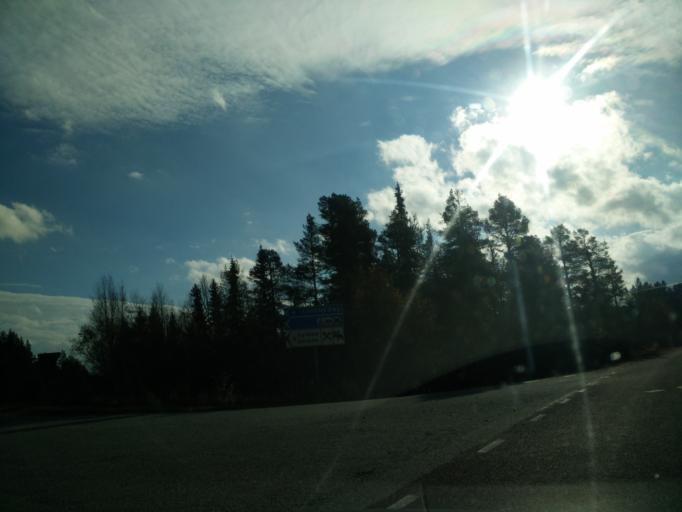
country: SE
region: Jaemtland
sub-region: Are Kommun
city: Are
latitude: 62.5563
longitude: 12.5681
